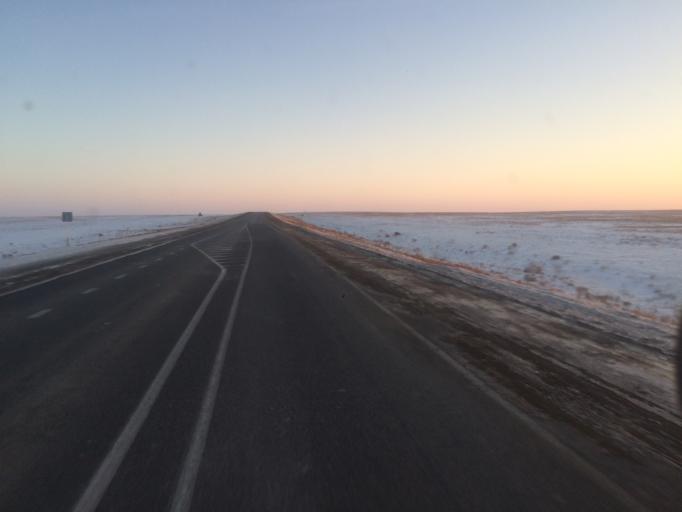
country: KZ
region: Qyzylorda
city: Sekseuil
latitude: 47.5729
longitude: 61.5110
